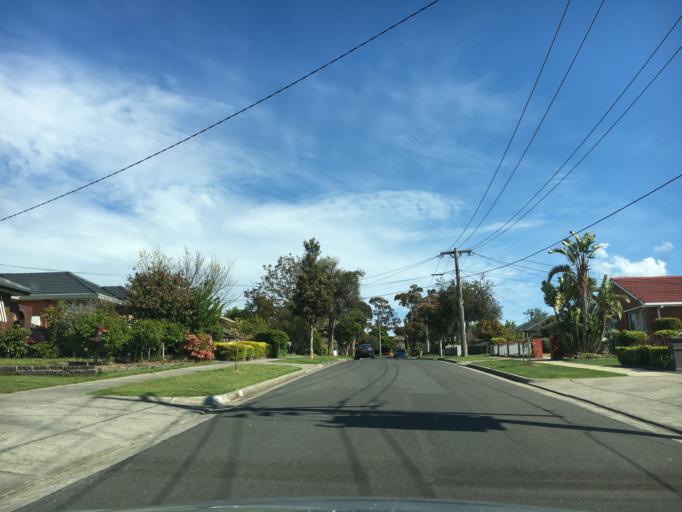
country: AU
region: Victoria
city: Clayton
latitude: -37.8928
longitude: 145.1193
